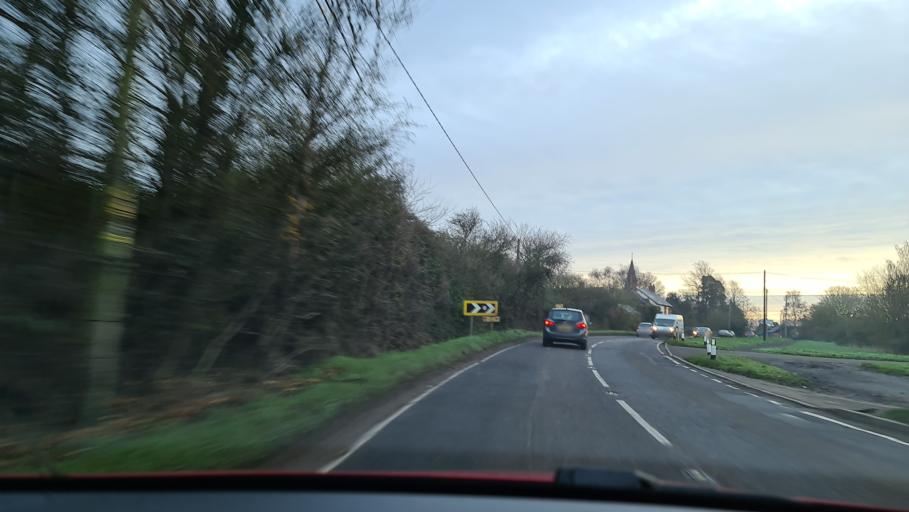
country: GB
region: England
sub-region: Buckinghamshire
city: Haddenham
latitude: 51.7542
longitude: -0.9273
